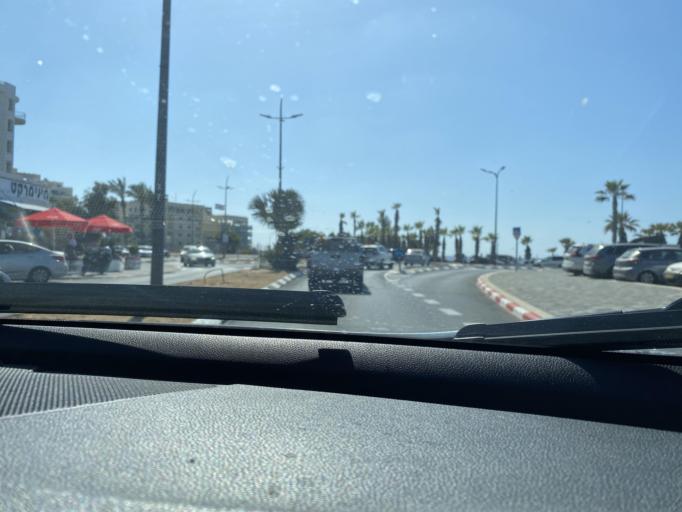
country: IL
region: Southern District
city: Ashqelon
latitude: 31.6838
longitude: 34.5616
